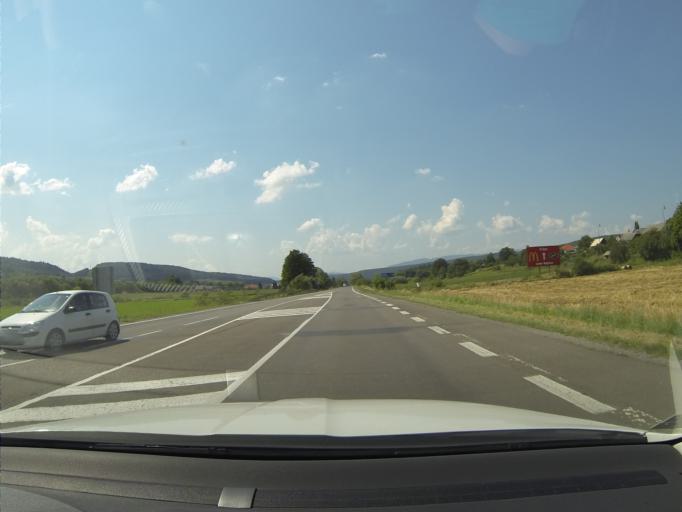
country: SK
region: Nitriansky
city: Handlova
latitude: 48.7775
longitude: 18.7107
